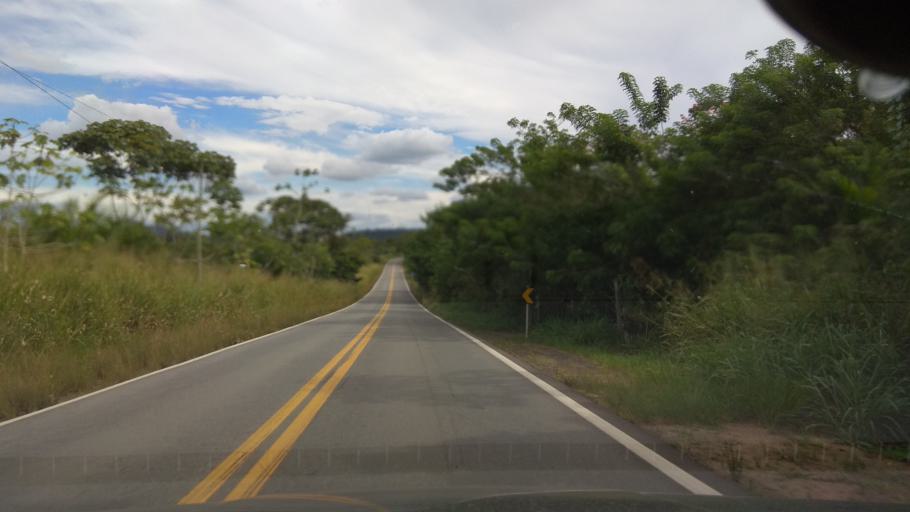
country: BR
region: Bahia
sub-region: Ubata
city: Ubata
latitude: -14.1990
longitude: -39.5683
